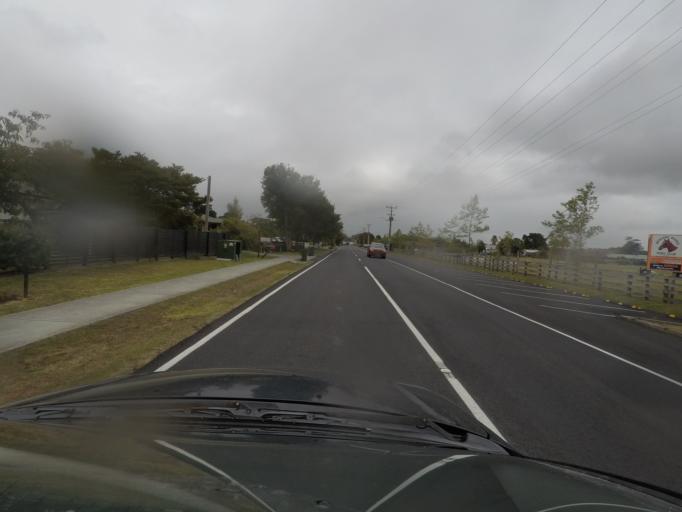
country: NZ
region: Auckland
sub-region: Auckland
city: Warkworth
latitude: -36.3483
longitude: 174.7127
